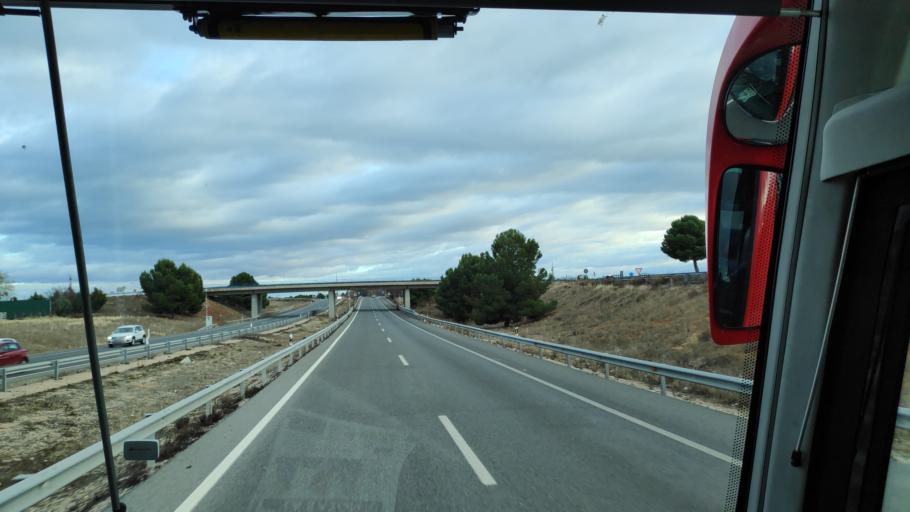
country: ES
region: Madrid
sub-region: Provincia de Madrid
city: Villarejo de Salvanes
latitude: 40.1727
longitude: -3.2935
